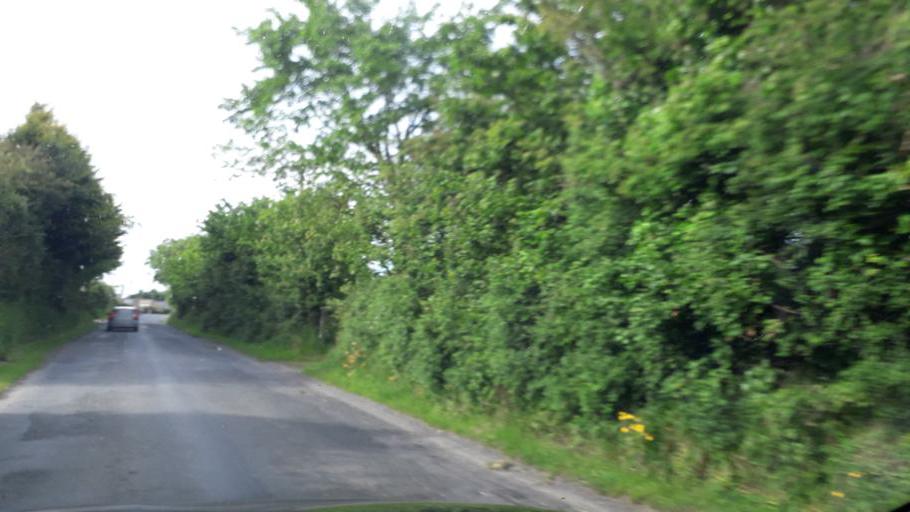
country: IE
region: Leinster
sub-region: Loch Garman
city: Courtown
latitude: 52.5811
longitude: -6.2307
